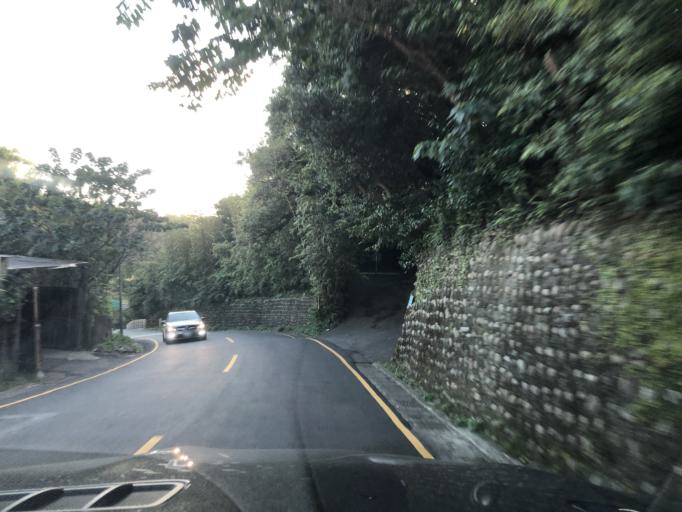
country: TW
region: Taipei
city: Taipei
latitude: 25.1434
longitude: 121.5569
